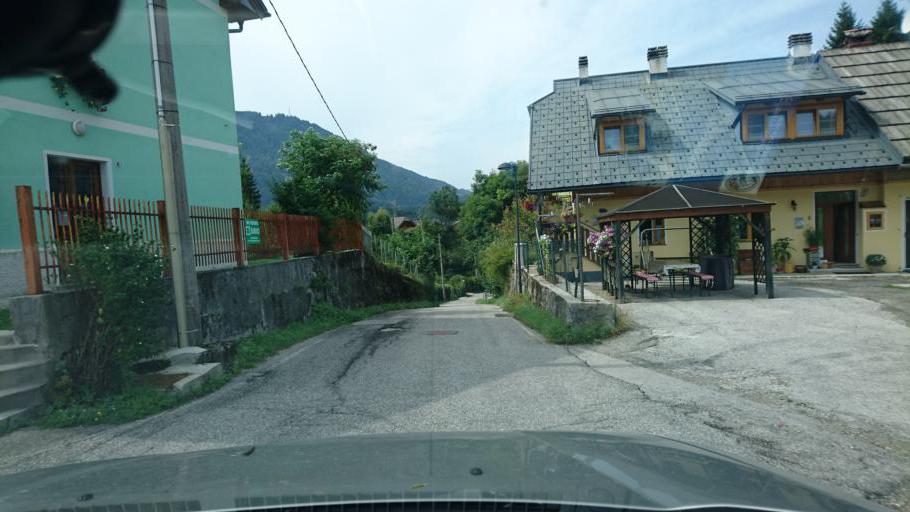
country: IT
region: Friuli Venezia Giulia
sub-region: Provincia di Udine
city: Tarvisio
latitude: 46.5039
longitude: 13.6024
